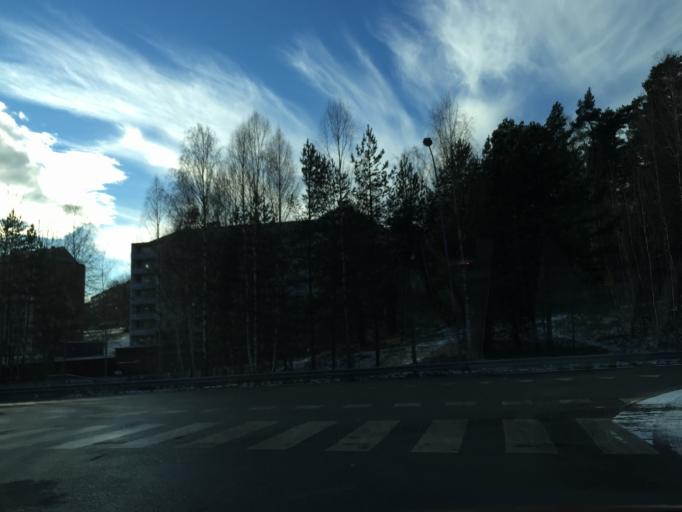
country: SE
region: Stockholm
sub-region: Sodertalje Kommun
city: Soedertaelje
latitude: 59.2087
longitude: 17.6001
